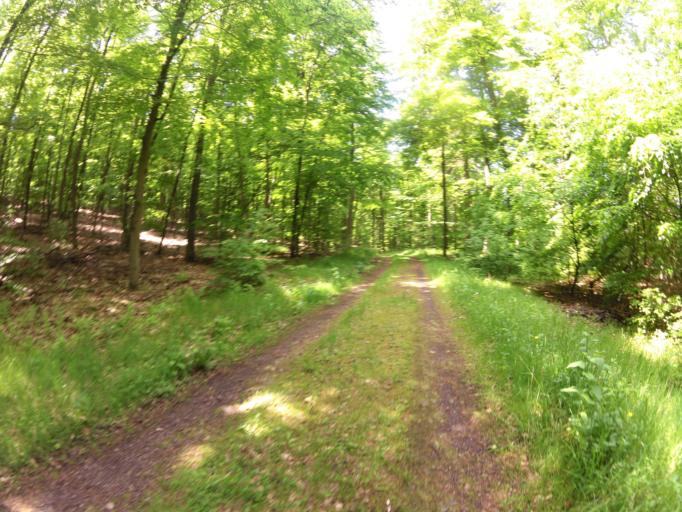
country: DE
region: Thuringia
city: Eisenach
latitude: 50.9535
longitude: 10.3002
